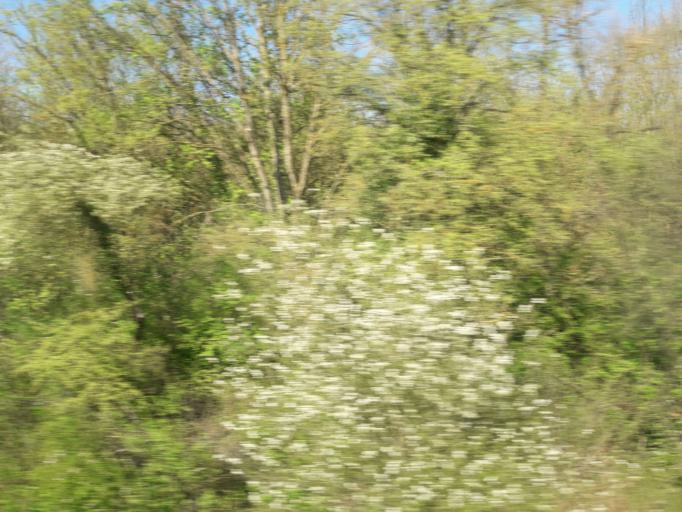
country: FR
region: Rhone-Alpes
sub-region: Departement de l'Isere
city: Saint-Lattier
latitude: 45.0827
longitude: 5.2178
